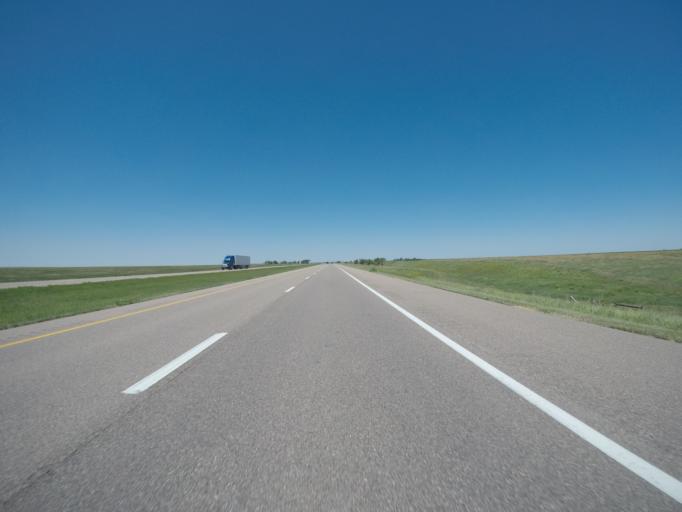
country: US
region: Kansas
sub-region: Gove County
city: Gove
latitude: 39.0879
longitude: -100.3052
